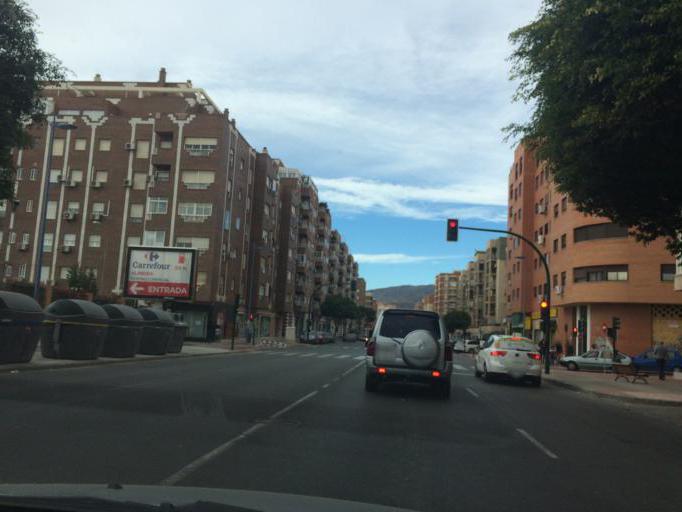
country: ES
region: Andalusia
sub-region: Provincia de Almeria
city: Almeria
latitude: 36.8432
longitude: -2.4447
